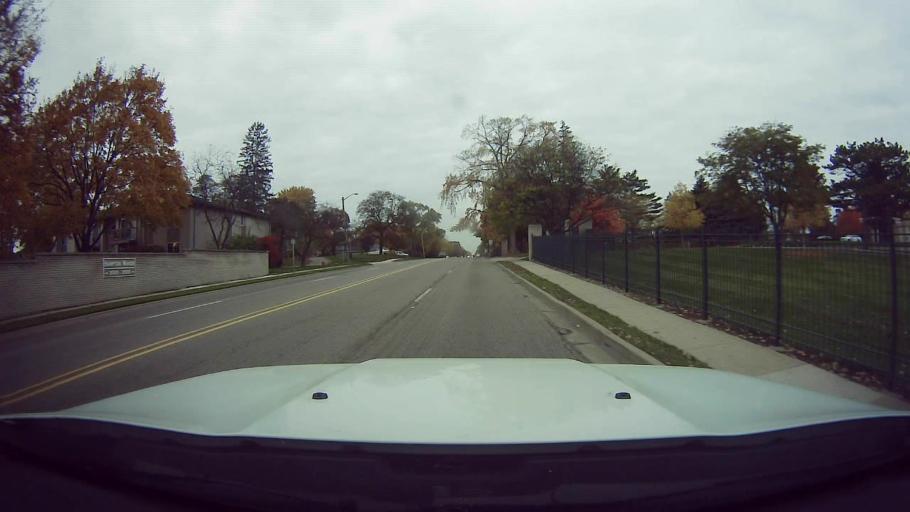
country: US
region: Michigan
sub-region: Oakland County
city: Birmingham
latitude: 42.5324
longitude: -83.1888
